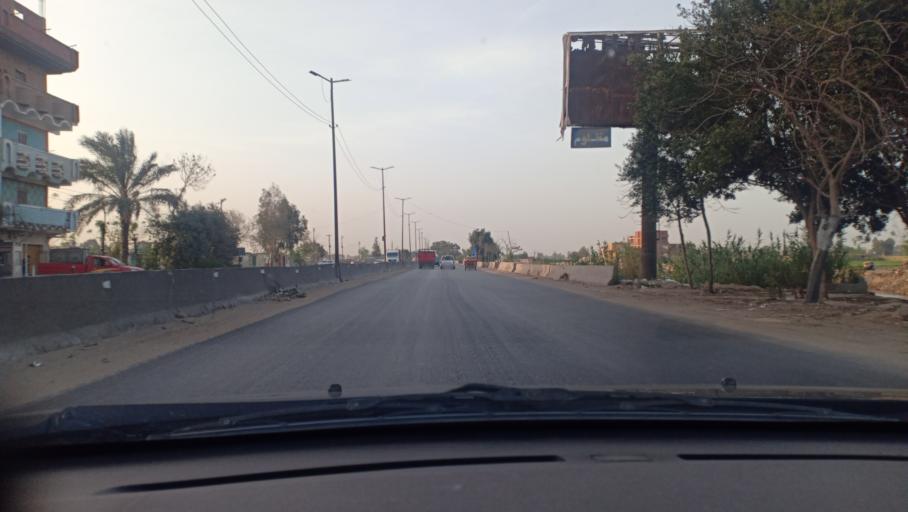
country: EG
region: Muhafazat al Minufiyah
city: Quwaysina
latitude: 30.5795
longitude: 31.2735
